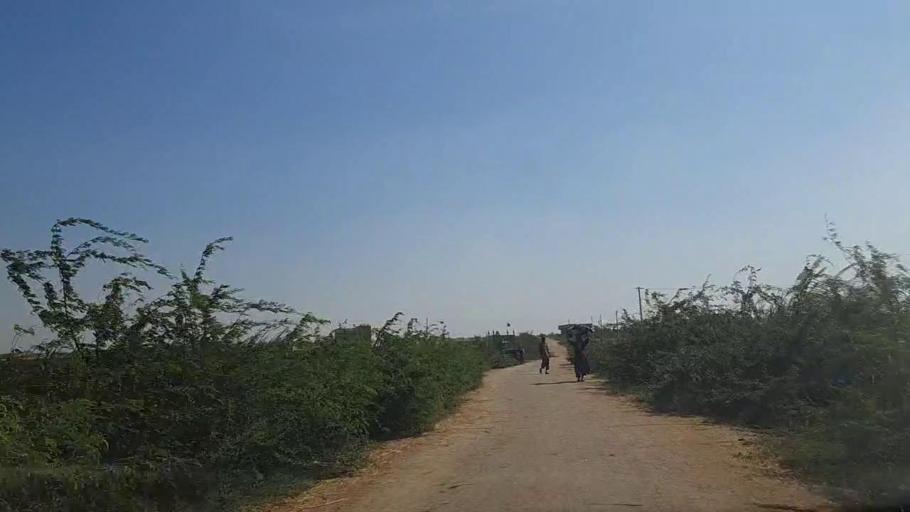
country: PK
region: Sindh
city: Thatta
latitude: 24.8238
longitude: 67.9922
